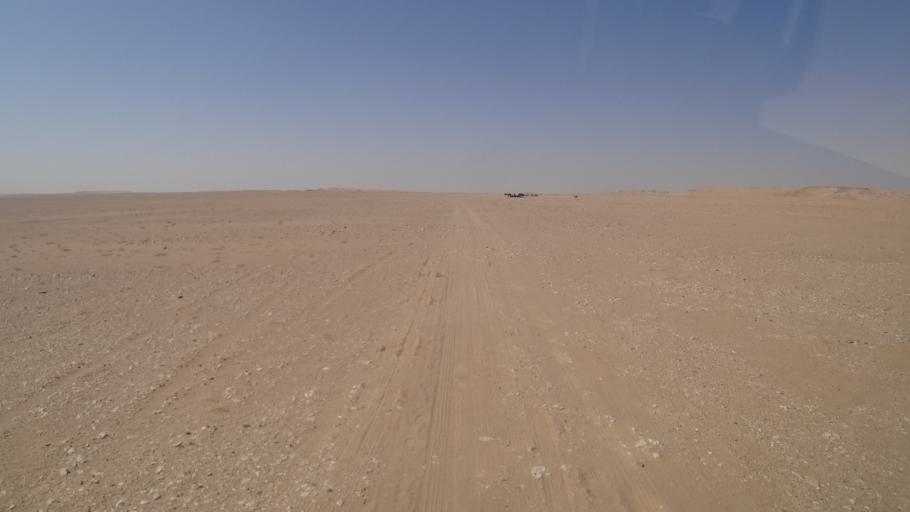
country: YE
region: Al Mahrah
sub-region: Shahan
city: Shihan as Sufla
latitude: 18.5758
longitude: 52.4995
